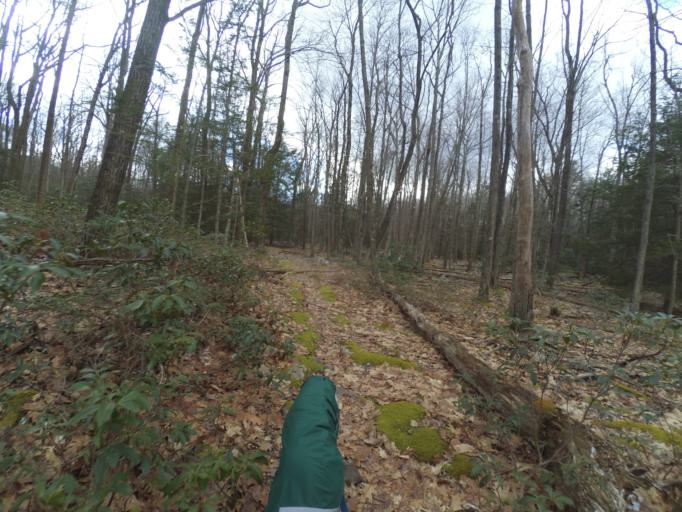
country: US
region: Pennsylvania
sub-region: Centre County
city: Boalsburg
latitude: 40.7412
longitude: -77.7290
